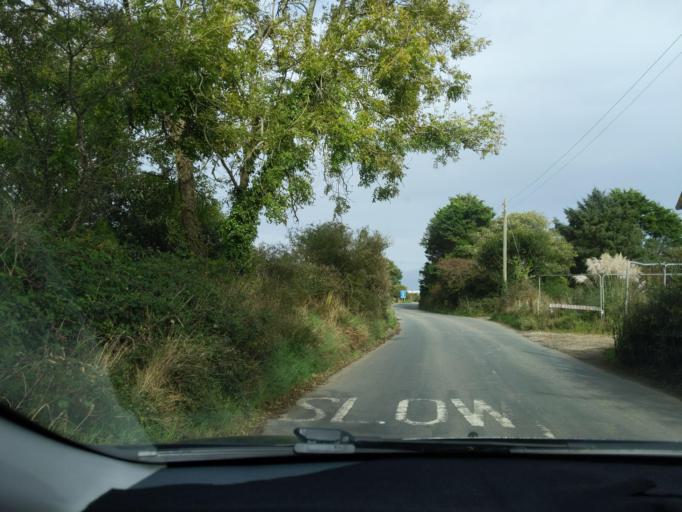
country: GB
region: England
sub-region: Cornwall
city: Mevagissey
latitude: 50.2450
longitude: -4.8051
